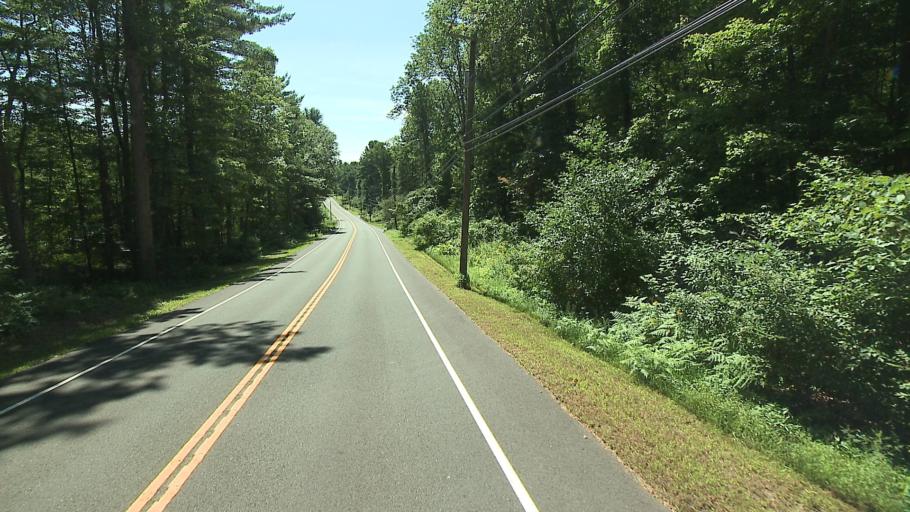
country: US
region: Connecticut
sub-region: Litchfield County
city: New Hartford Center
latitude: 41.9200
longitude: -72.9734
